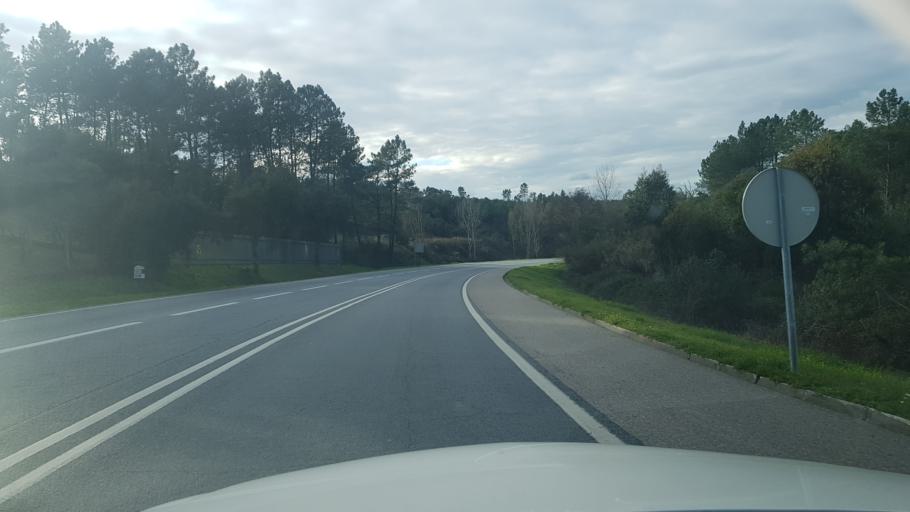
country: PT
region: Santarem
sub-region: Abrantes
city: Abrantes
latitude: 39.4644
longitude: -8.2189
